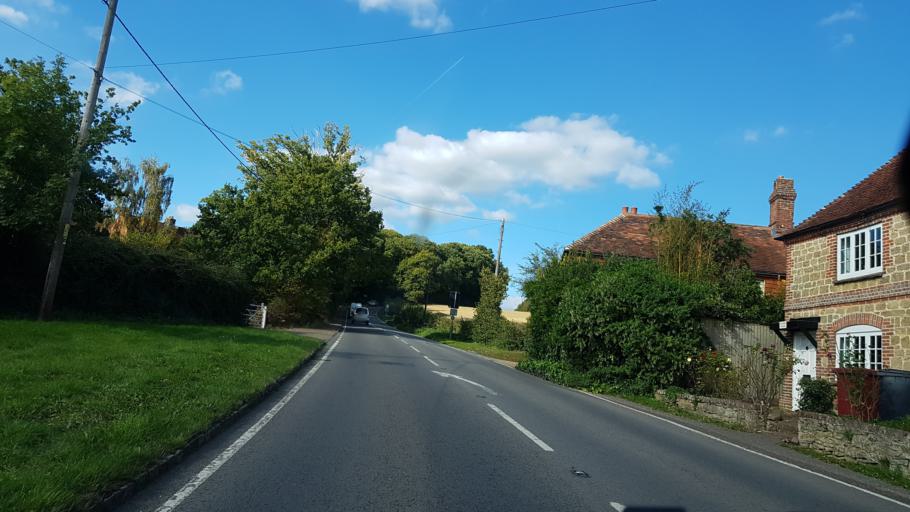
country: GB
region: England
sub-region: Surrey
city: Chiddingfold
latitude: 51.0589
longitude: -0.6429
